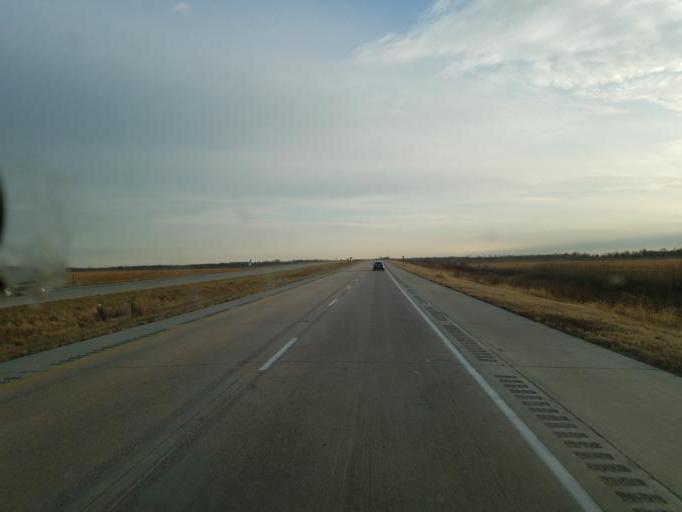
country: US
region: Nebraska
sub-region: Burt County
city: Tekamah
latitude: 41.8694
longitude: -96.1038
